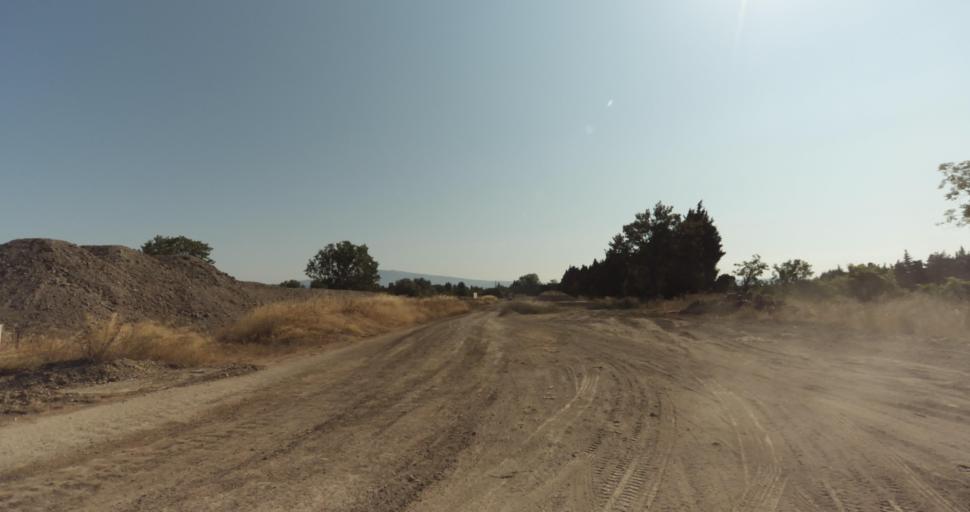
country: FR
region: Provence-Alpes-Cote d'Azur
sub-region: Departement du Vaucluse
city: Althen-des-Paluds
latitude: 44.0141
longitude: 4.9708
